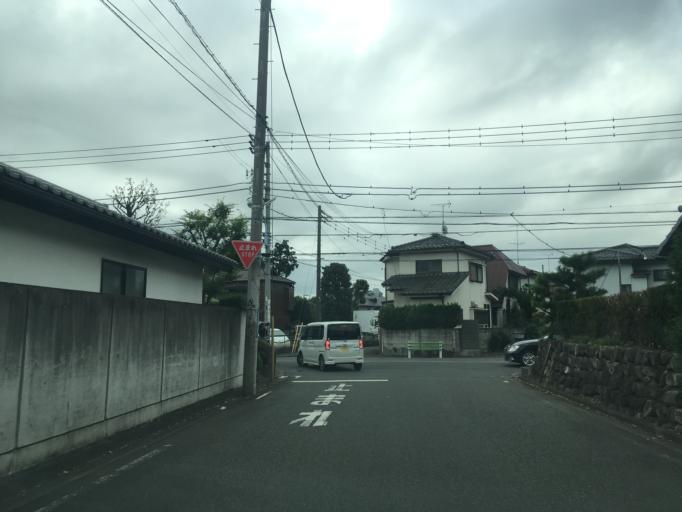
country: JP
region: Tokyo
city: Hino
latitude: 35.7262
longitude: 139.3914
